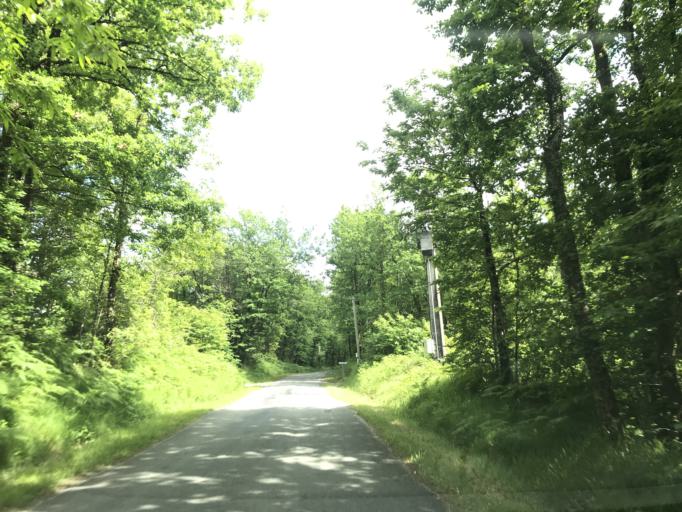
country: FR
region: Poitou-Charentes
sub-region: Departement de la Charente
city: Chalais
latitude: 45.2764
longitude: 0.1066
